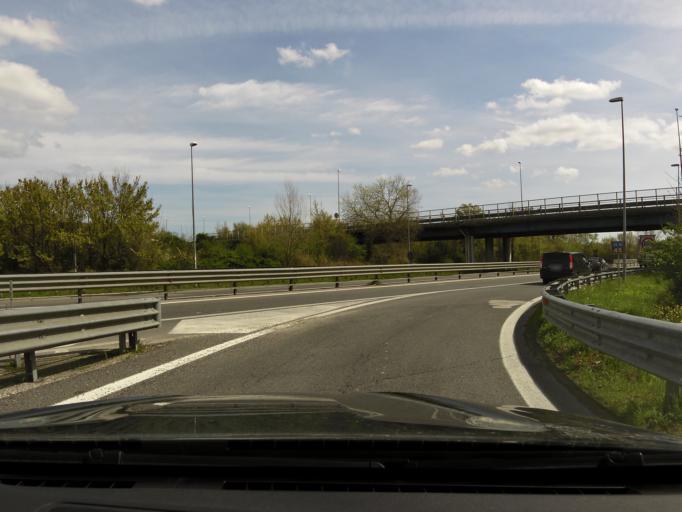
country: IT
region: The Marches
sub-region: Provincia di Ancona
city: San Biagio
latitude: 43.5340
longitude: 13.5133
